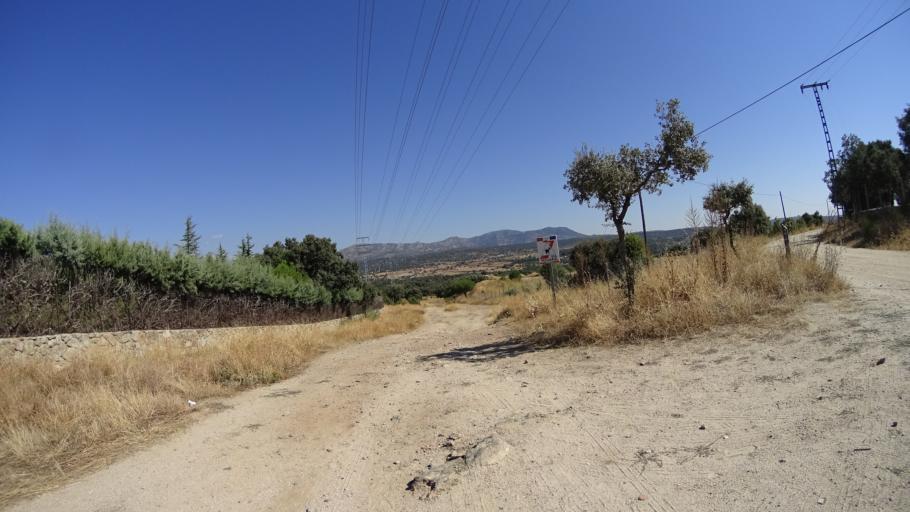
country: ES
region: Madrid
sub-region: Provincia de Madrid
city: Galapagar
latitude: 40.5981
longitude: -4.0003
